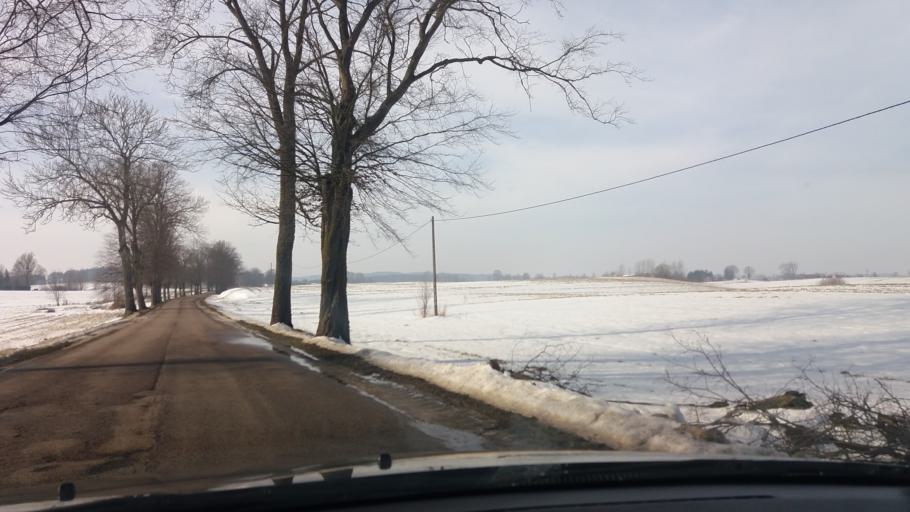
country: PL
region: Warmian-Masurian Voivodeship
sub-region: Powiat olsztynski
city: Jeziorany
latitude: 54.1032
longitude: 20.7188
